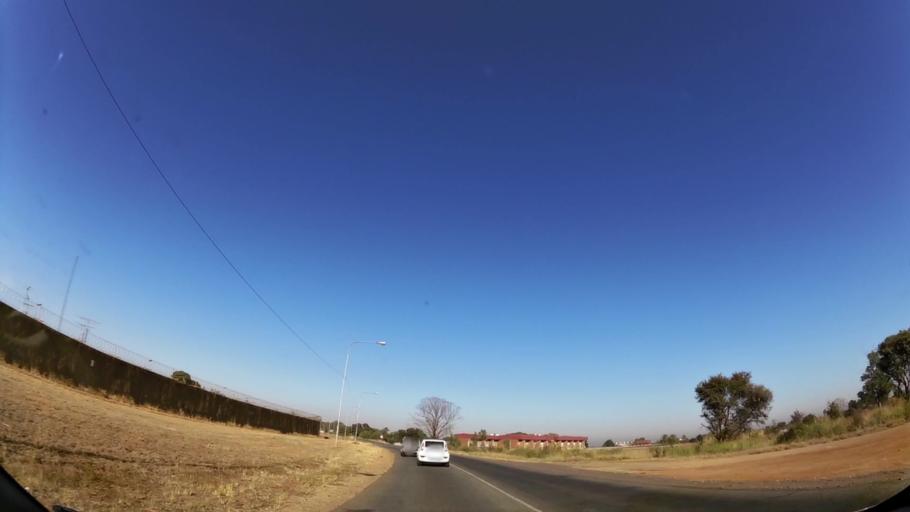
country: ZA
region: Gauteng
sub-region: City of Tshwane Metropolitan Municipality
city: Centurion
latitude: -25.8107
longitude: 28.2118
